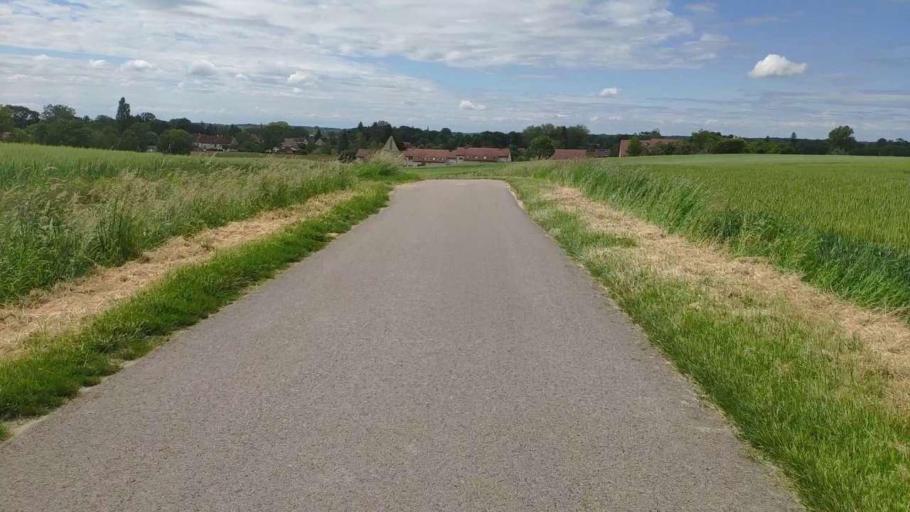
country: FR
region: Franche-Comte
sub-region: Departement du Jura
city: Bletterans
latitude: 46.7373
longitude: 5.5074
